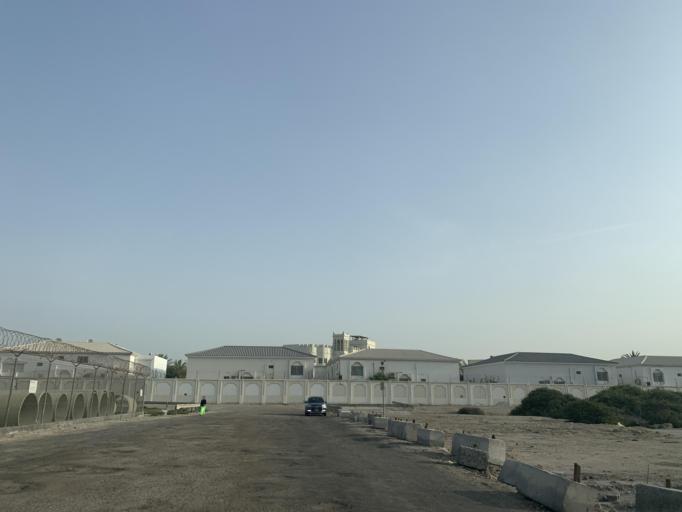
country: BH
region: Manama
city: Jidd Hafs
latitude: 26.1964
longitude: 50.5595
